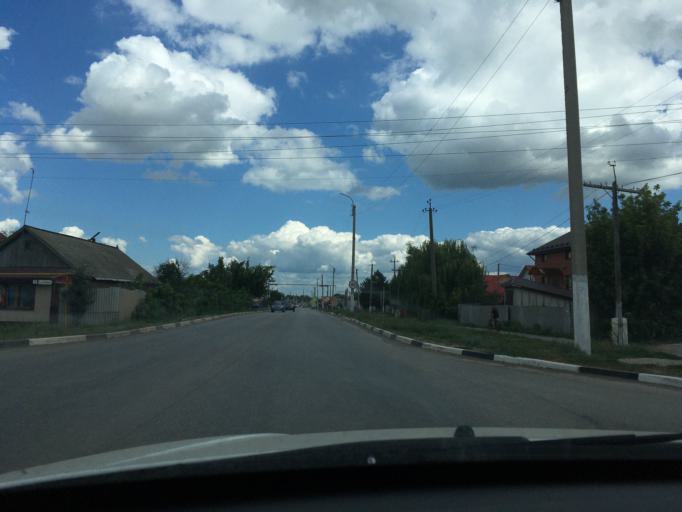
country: RU
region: Samara
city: Bezenchuk
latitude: 52.9891
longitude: 49.4355
